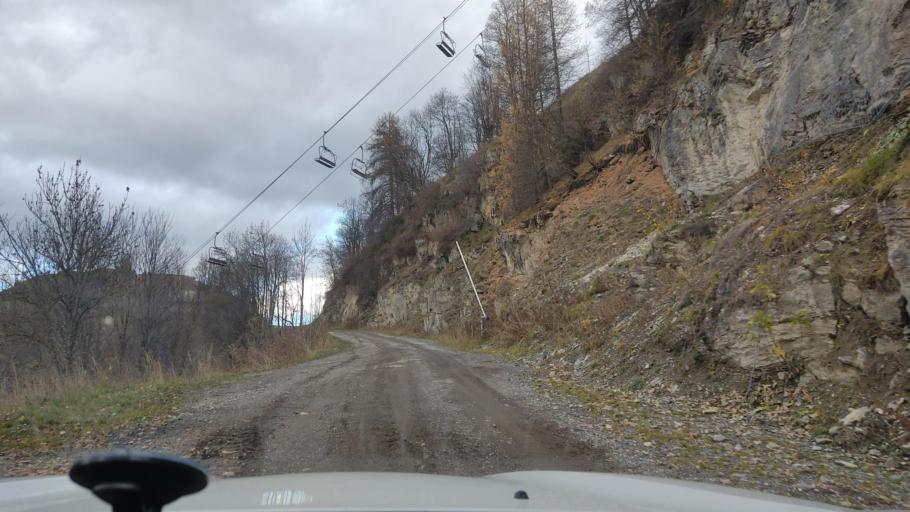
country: FR
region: Rhone-Alpes
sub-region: Departement de la Savoie
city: Valloire
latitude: 45.1560
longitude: 6.4235
